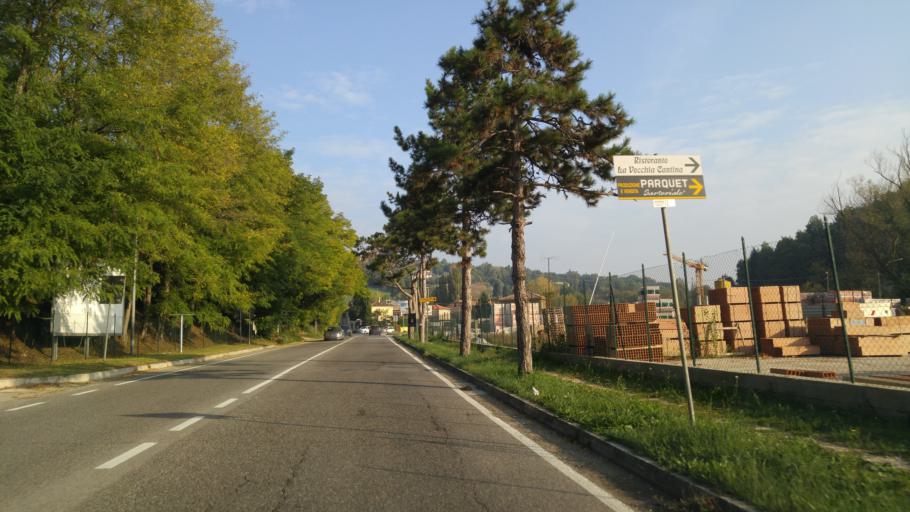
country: IT
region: The Marches
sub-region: Provincia di Pesaro e Urbino
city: Pesaro
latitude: 43.8877
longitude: 12.9310
